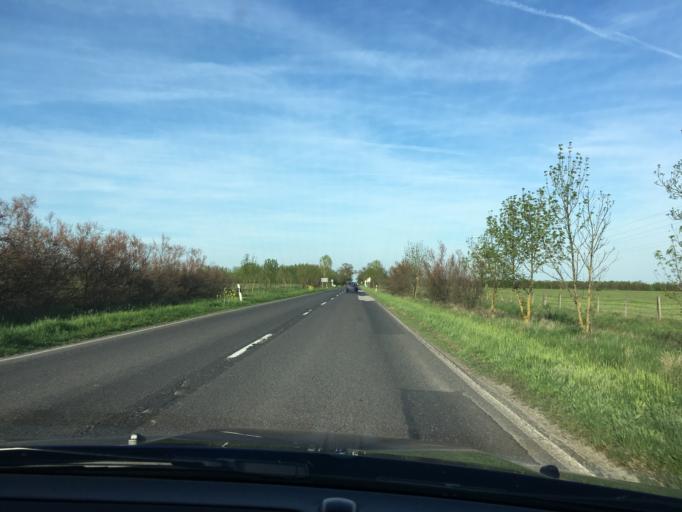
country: HU
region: Bekes
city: Szeghalom
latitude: 47.0065
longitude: 21.2314
